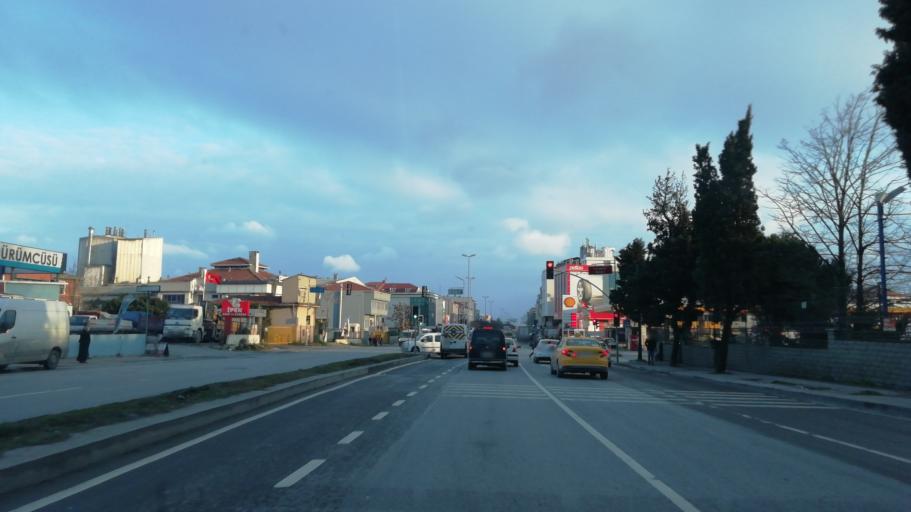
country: TR
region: Istanbul
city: Esenyurt
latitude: 41.0102
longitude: 28.7009
